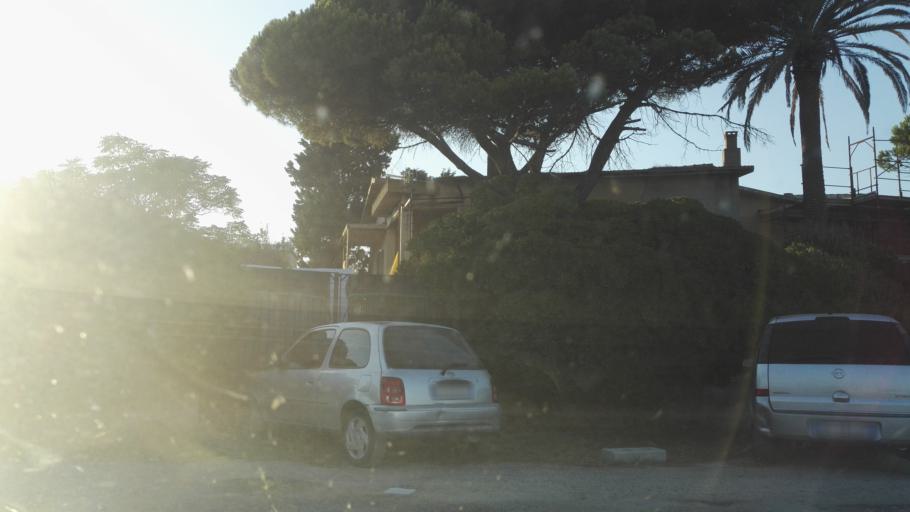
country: IT
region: Calabria
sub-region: Provincia di Reggio Calabria
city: Siderno
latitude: 38.2708
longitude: 16.3029
